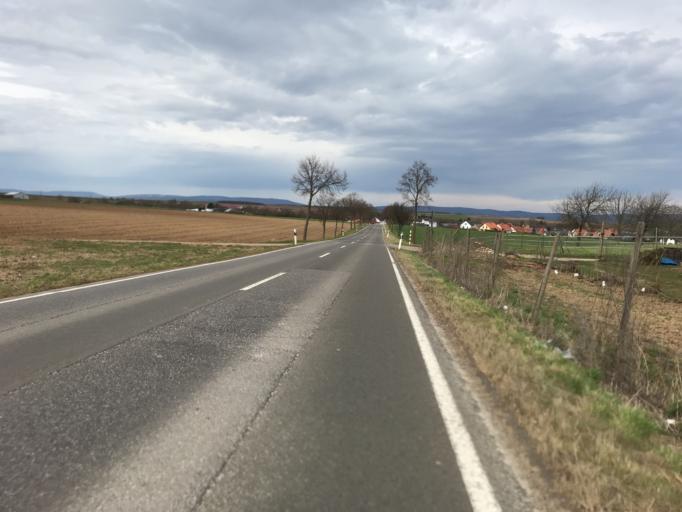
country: DE
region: Rheinland-Pfalz
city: Ober-Hilbersheim
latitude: 49.8937
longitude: 8.0343
